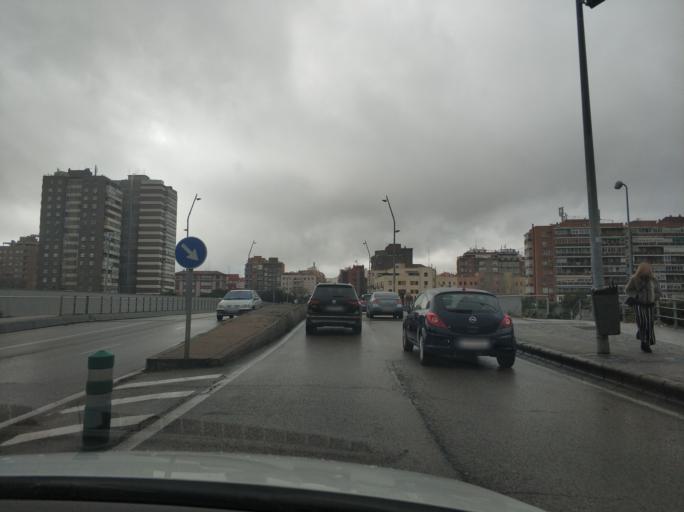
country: ES
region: Madrid
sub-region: Provincia de Madrid
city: Usera
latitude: 40.3897
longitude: -3.6974
